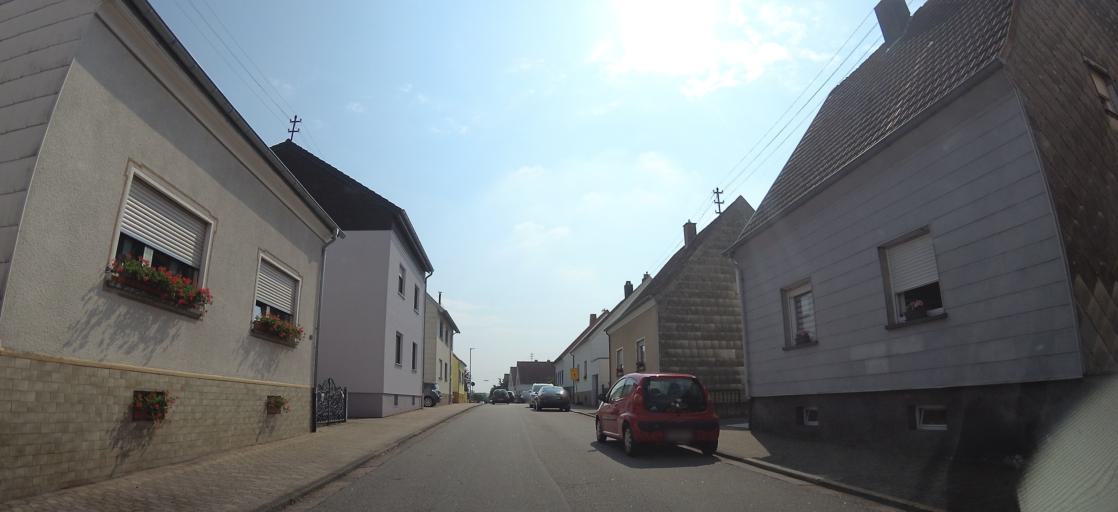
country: DE
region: Saarland
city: Bexbach
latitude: 49.3529
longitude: 7.2636
